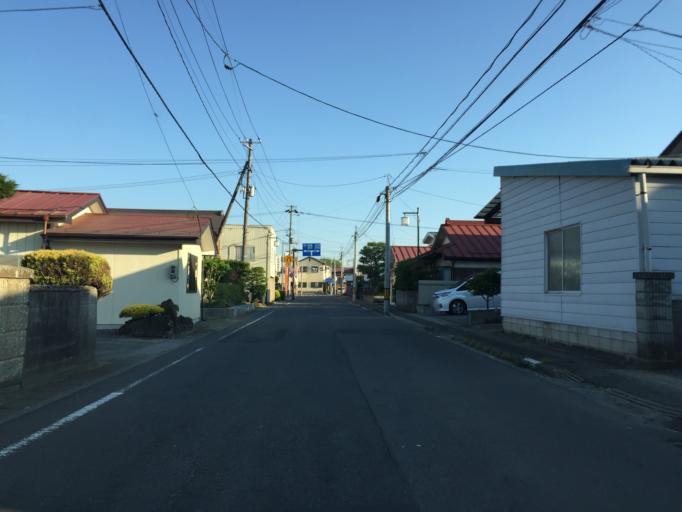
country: JP
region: Fukushima
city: Ishikawa
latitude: 37.0826
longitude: 140.4164
